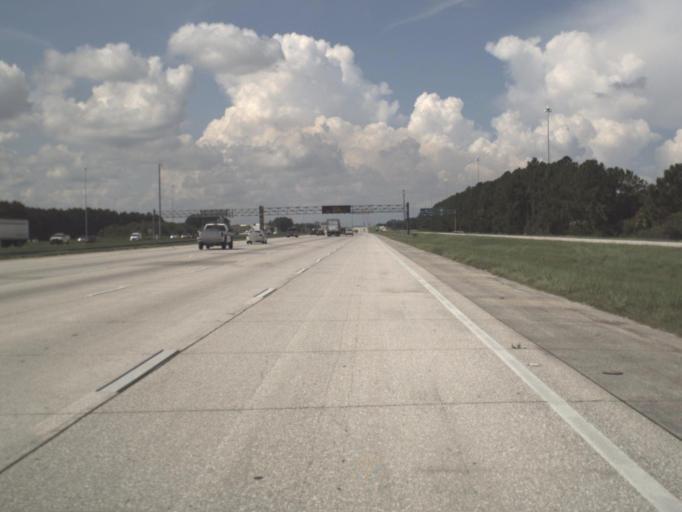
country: US
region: Florida
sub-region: Hillsborough County
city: Progress Village
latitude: 27.9164
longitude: -82.3370
